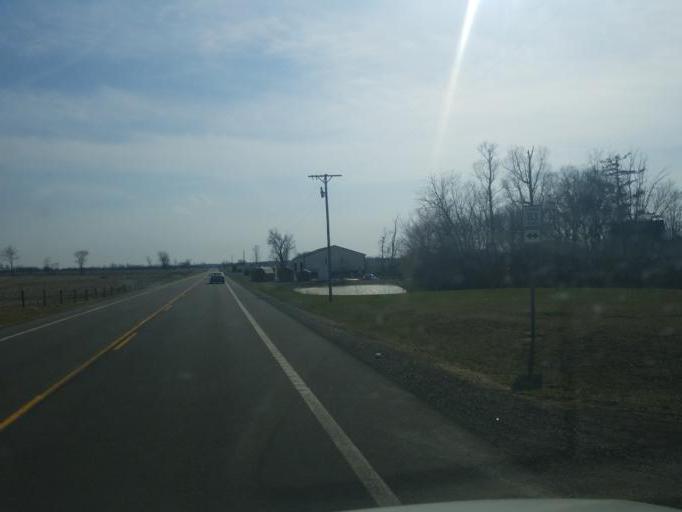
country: US
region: Ohio
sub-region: Logan County
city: Northwood
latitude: 40.4654
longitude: -83.7162
